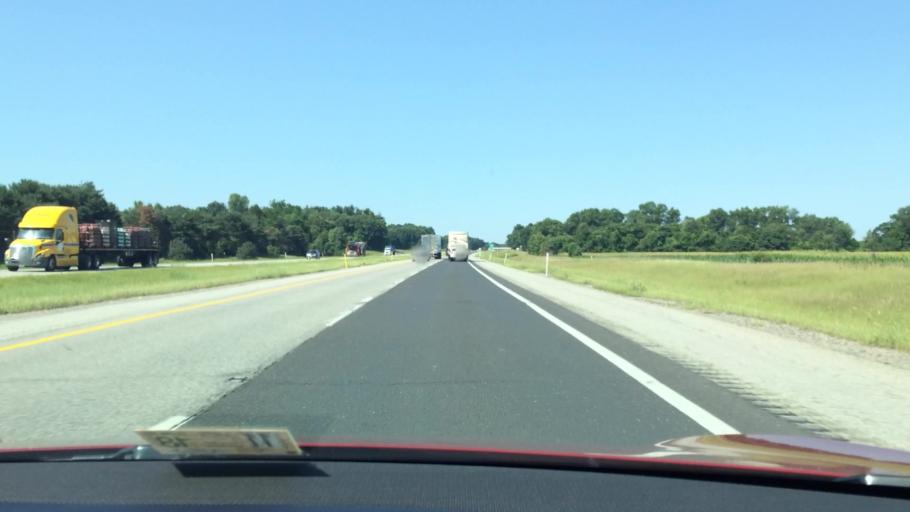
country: US
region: Indiana
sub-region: Elkhart County
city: Middlebury
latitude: 41.7366
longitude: -85.7417
